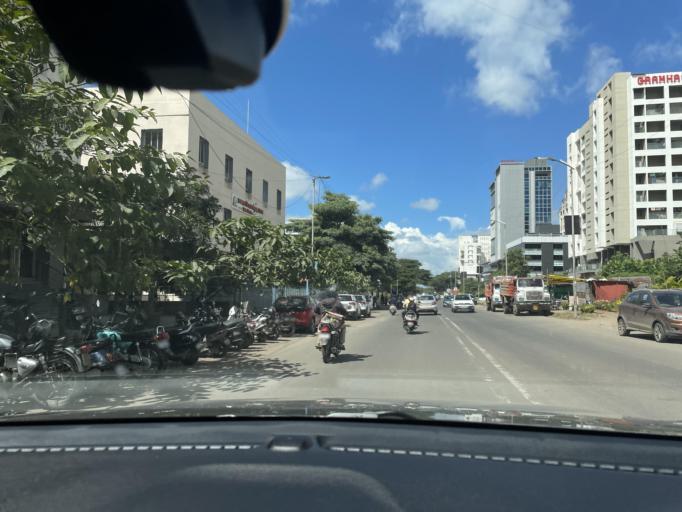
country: IN
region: Maharashtra
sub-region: Pune Division
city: Shivaji Nagar
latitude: 18.5208
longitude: 73.7791
